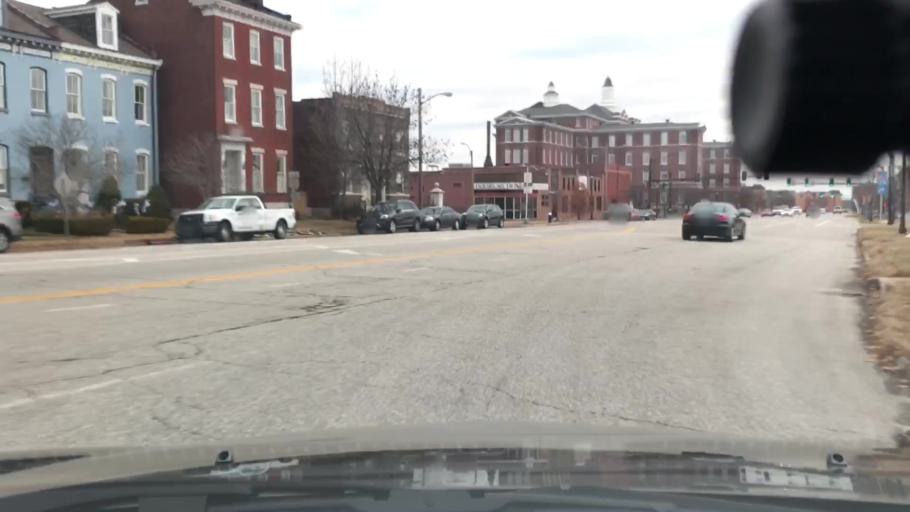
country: US
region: Missouri
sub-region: City of Saint Louis
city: St. Louis
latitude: 38.6136
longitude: -90.2115
